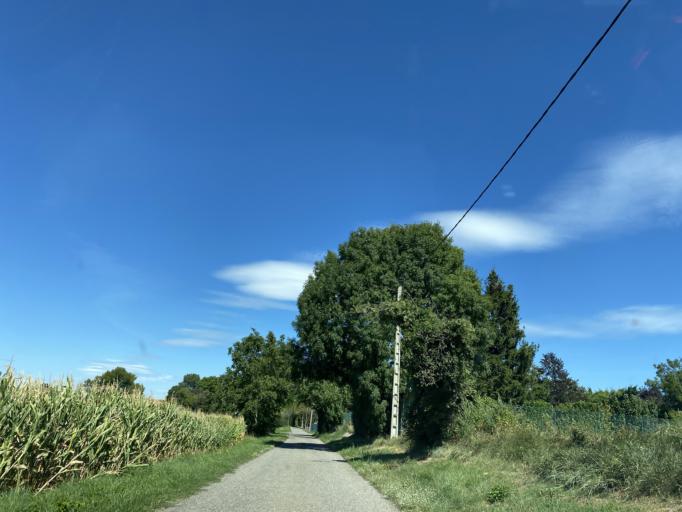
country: FR
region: Auvergne
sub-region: Departement du Puy-de-Dome
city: Perignat-les-Sarlieve
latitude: 45.7650
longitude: 3.1445
